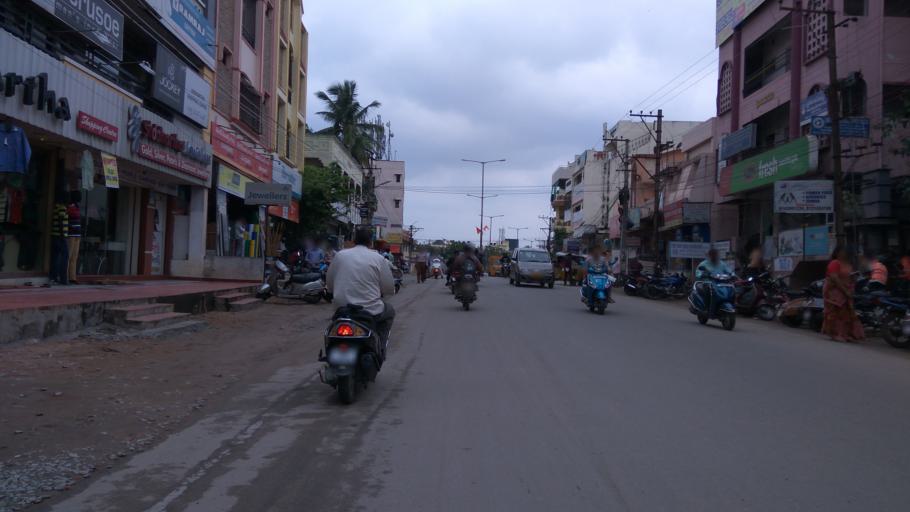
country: IN
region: Telangana
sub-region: Hyderabad
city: Malkajgiri
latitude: 17.4562
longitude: 78.5362
